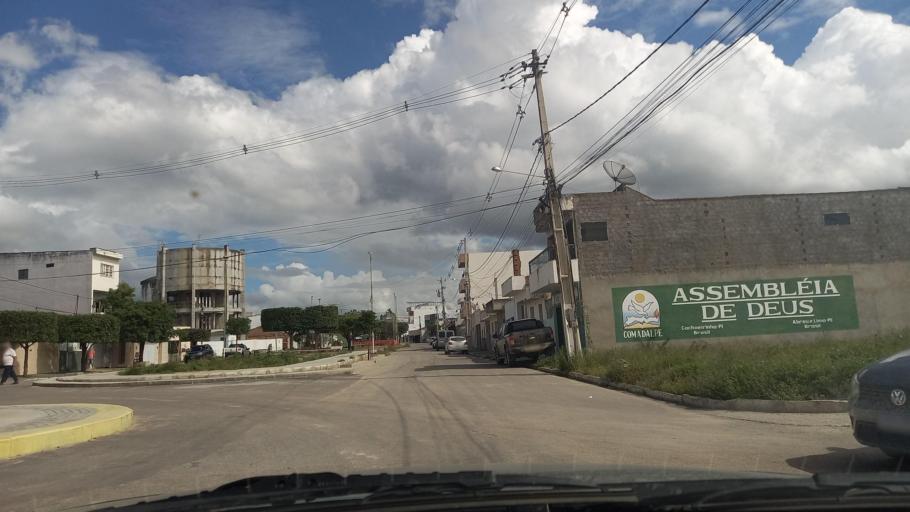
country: BR
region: Pernambuco
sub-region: Cachoeirinha
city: Cachoeirinha
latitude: -8.4913
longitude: -36.2381
